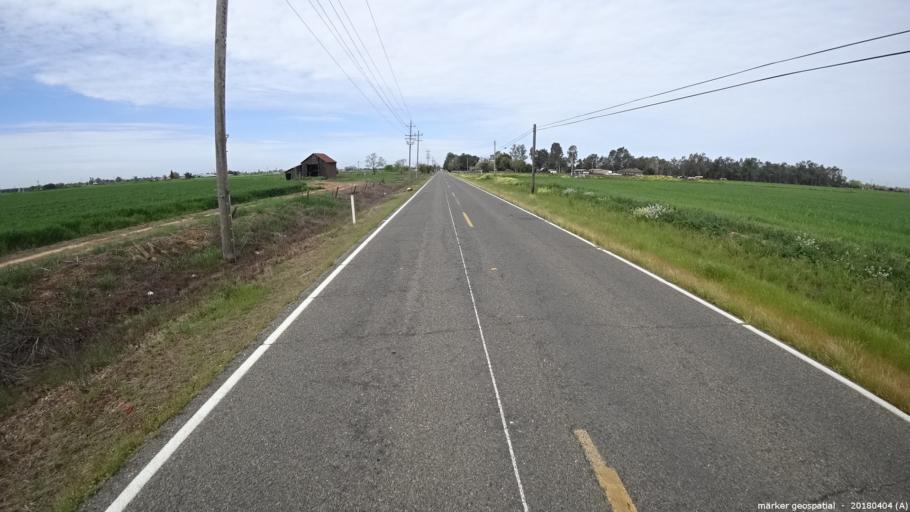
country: US
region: California
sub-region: Sacramento County
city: Galt
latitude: 38.2623
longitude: -121.2771
